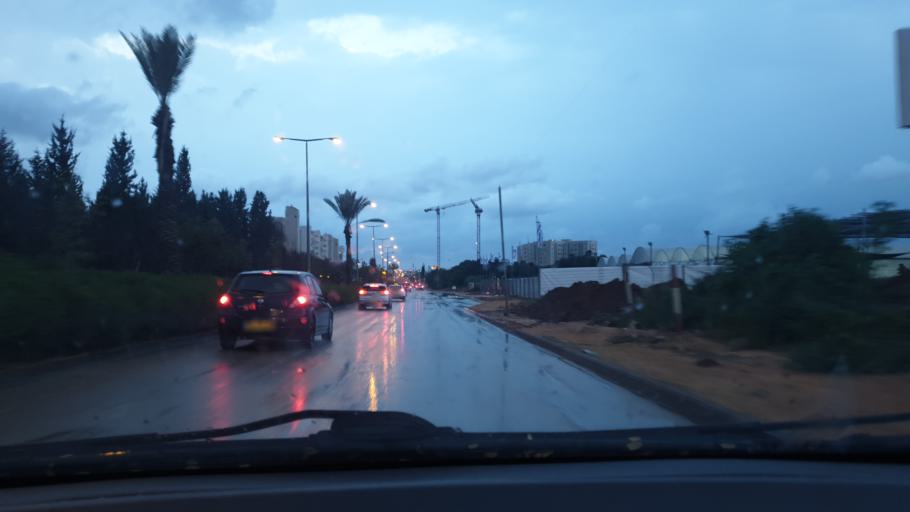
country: IL
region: Central District
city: Bet Dagan
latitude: 31.9728
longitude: 34.8203
